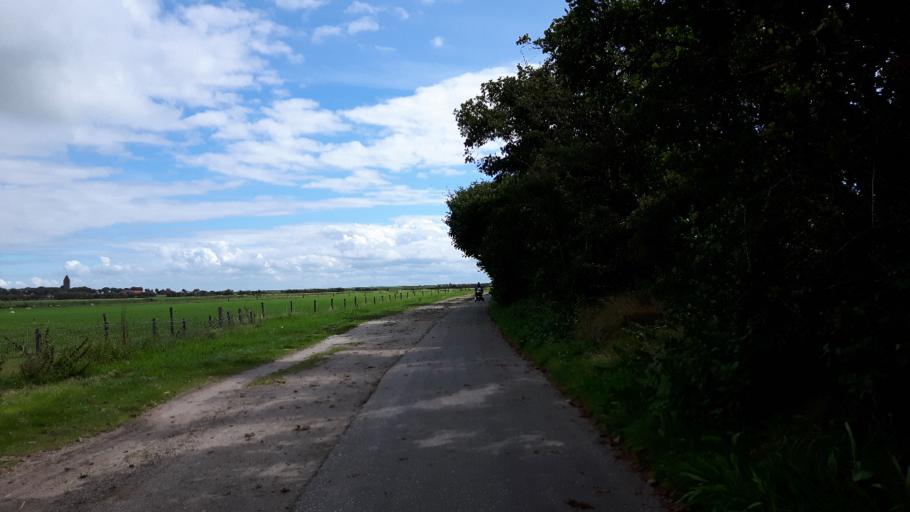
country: NL
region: Friesland
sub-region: Gemeente Ameland
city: Hollum
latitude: 53.4389
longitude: 5.6228
